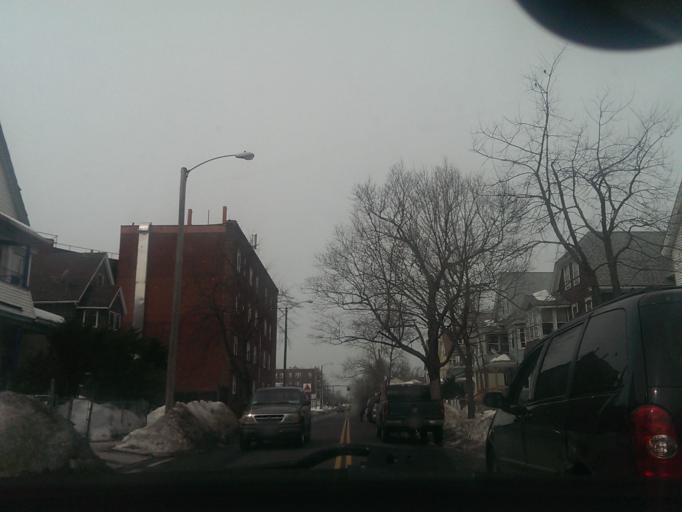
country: US
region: Massachusetts
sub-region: Hampden County
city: Springfield
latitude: 42.0922
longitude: -72.5555
